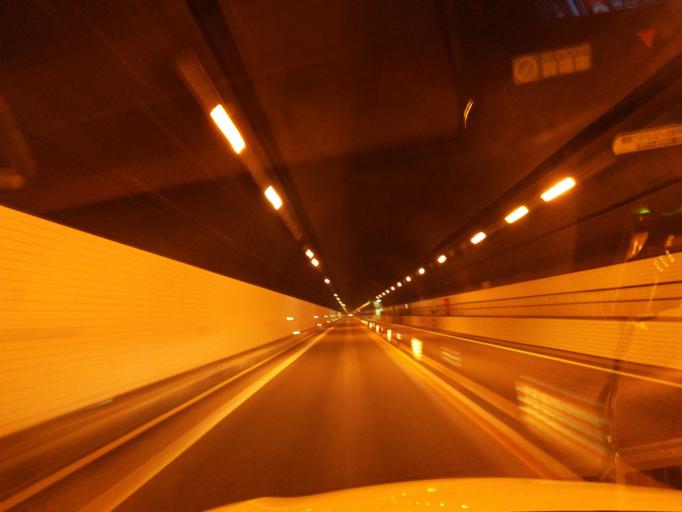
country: JP
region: Tokushima
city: Ikedacho
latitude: 34.0168
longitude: 133.7543
